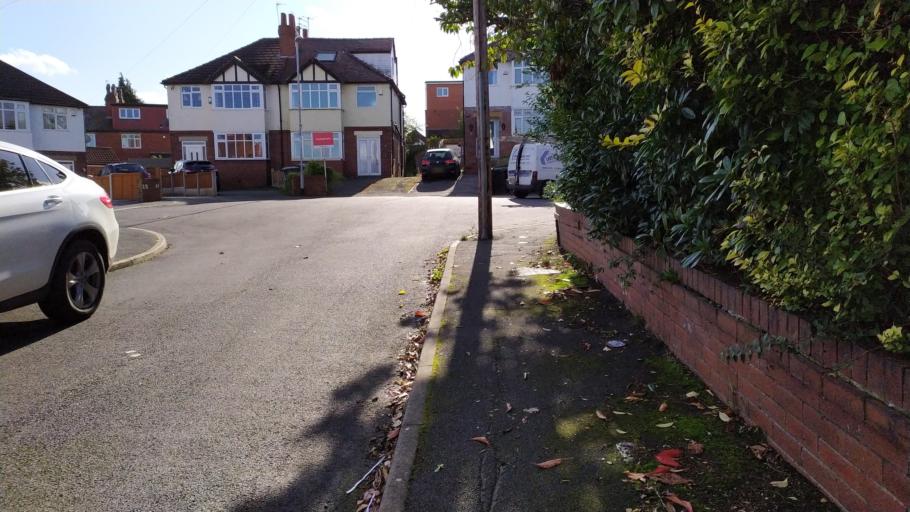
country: GB
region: England
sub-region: City and Borough of Leeds
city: Leeds
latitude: 53.8238
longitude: -1.5843
